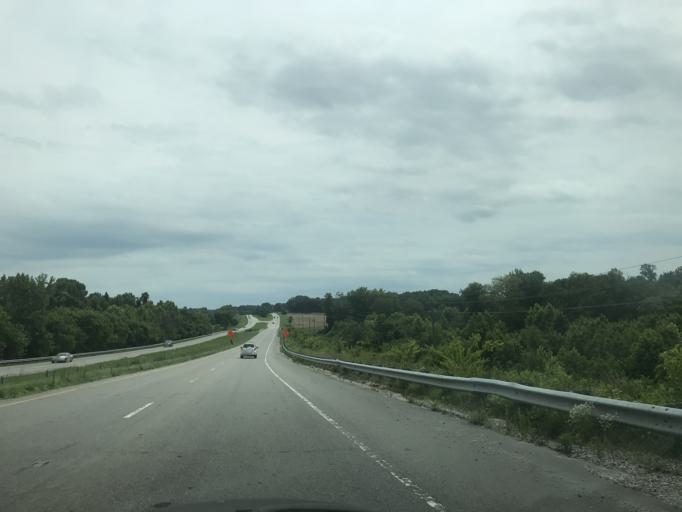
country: US
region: North Carolina
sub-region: Franklin County
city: Franklinton
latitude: 36.1720
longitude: -78.4484
